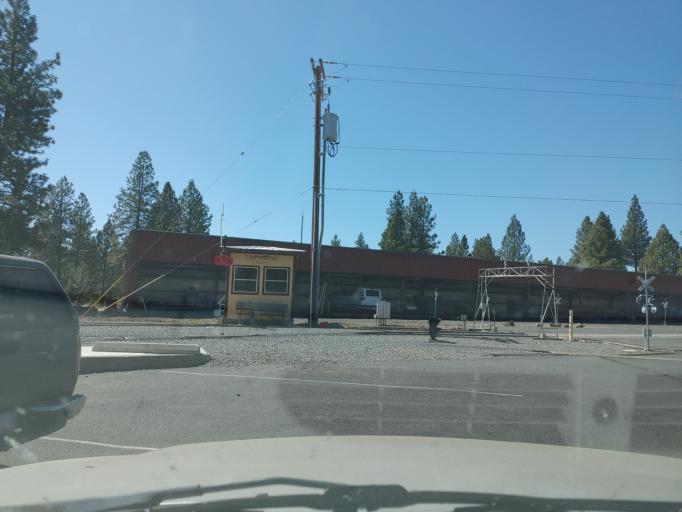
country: US
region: Oregon
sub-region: Klamath County
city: Klamath Falls
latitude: 42.5571
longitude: -121.8867
